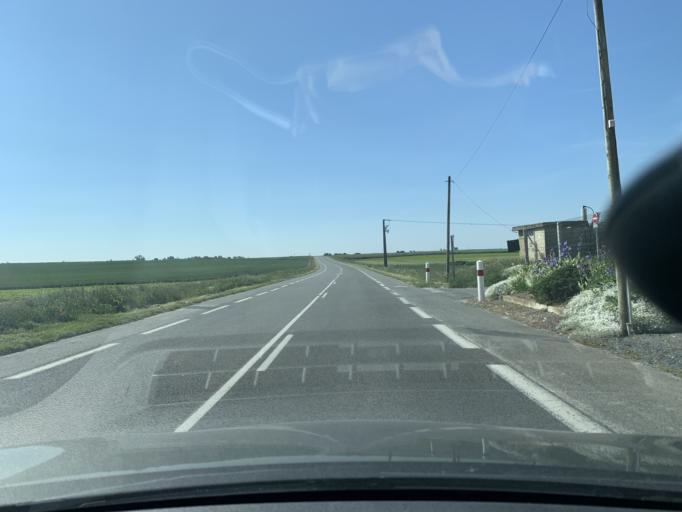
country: FR
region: Nord-Pas-de-Calais
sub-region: Departement du Nord
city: Cambrai
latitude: 50.1474
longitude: 3.2431
